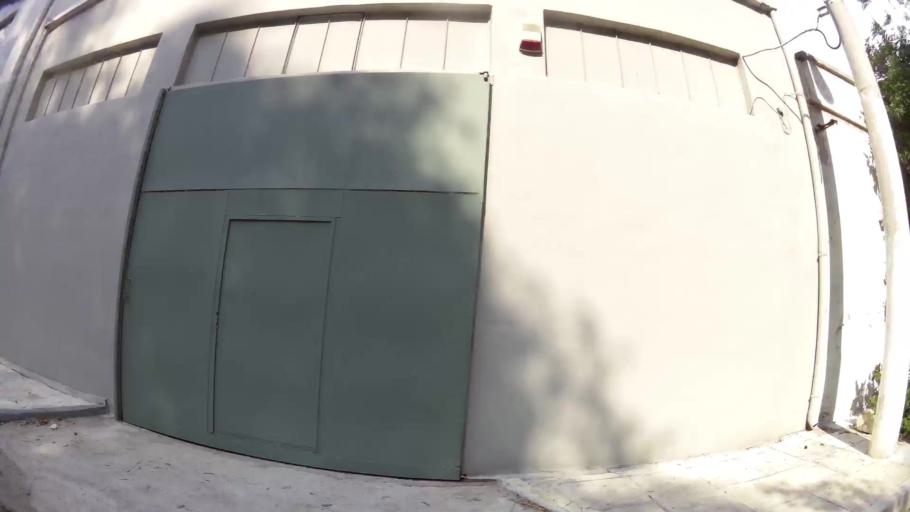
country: GR
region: Attica
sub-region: Nomos Piraios
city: Agios Ioannis Rentis
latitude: 37.9491
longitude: 23.6621
